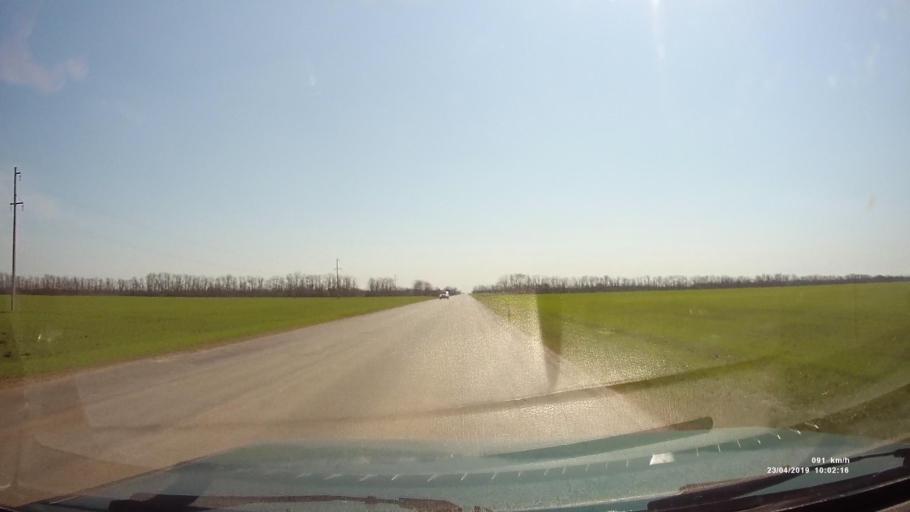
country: RU
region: Rostov
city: Sovetskoye
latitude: 46.7614
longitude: 42.1654
